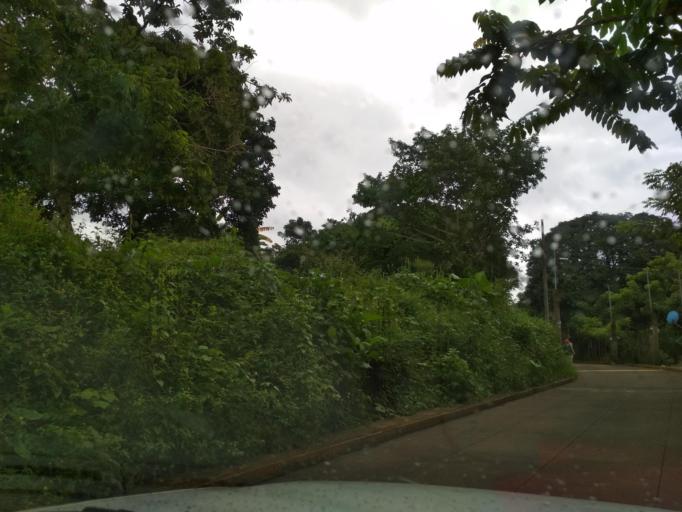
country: MX
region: Veracruz
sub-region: San Andres Tuxtla
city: Tonalapan
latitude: 18.4564
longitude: -95.2266
